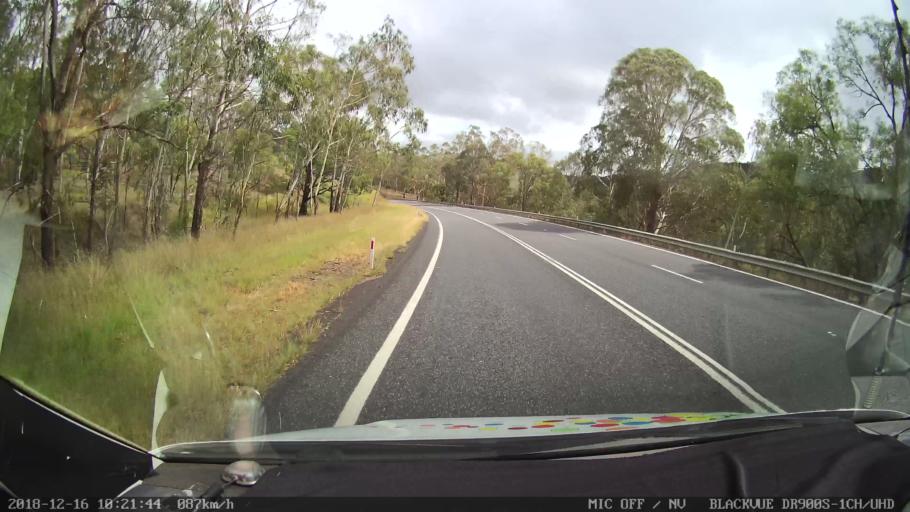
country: AU
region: New South Wales
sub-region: Tenterfield Municipality
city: Carrolls Creek
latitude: -29.2032
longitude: 152.0140
